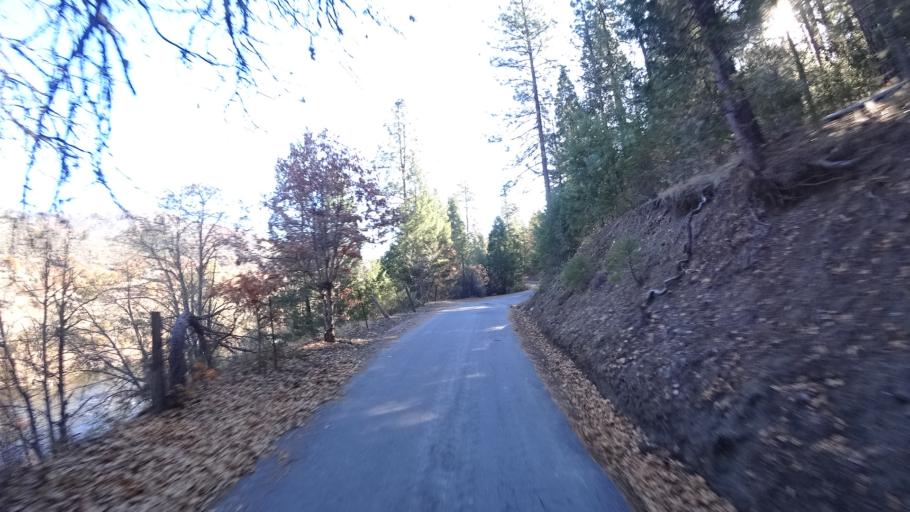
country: US
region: California
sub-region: Siskiyou County
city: Yreka
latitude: 41.8419
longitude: -122.8833
